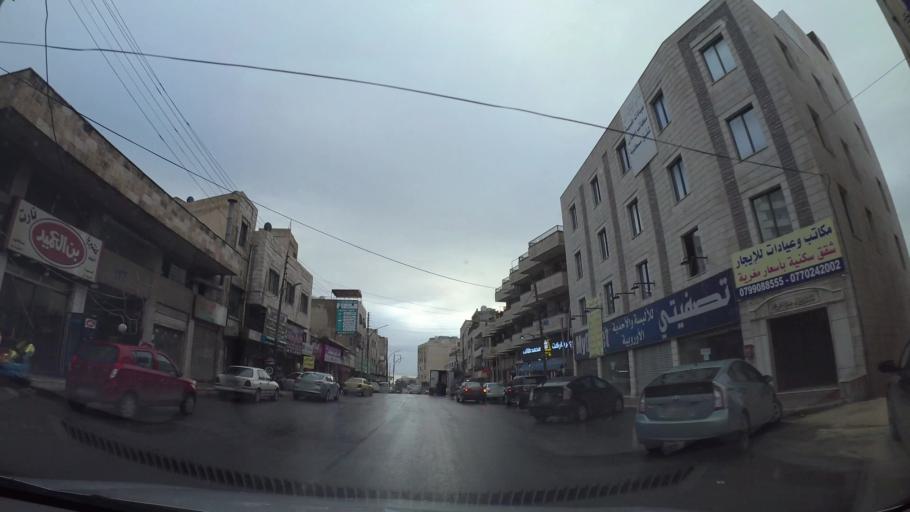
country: JO
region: Amman
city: Al Jubayhah
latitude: 32.0286
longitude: 35.8356
